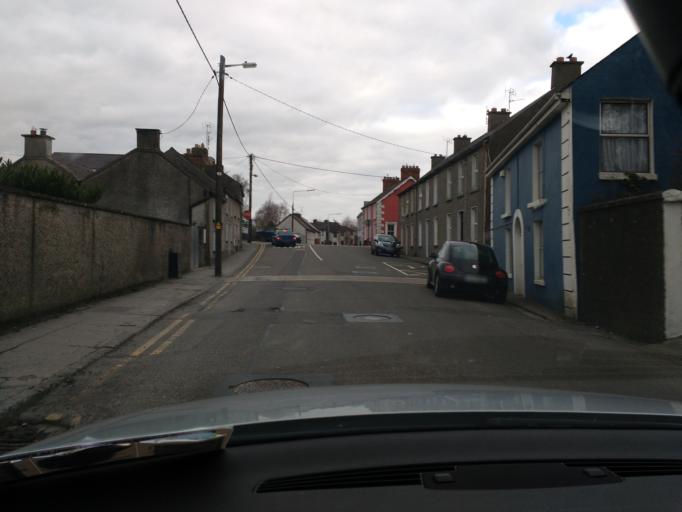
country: IE
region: Leinster
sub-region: Kilkenny
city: Kilkenny
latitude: 52.6578
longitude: -7.2524
